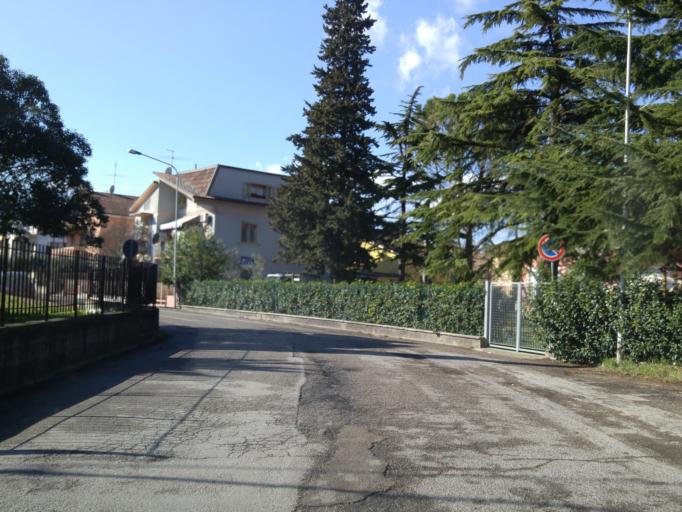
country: IT
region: The Marches
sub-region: Provincia di Pesaro e Urbino
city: Fossombrone
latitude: 43.6857
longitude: 12.8028
